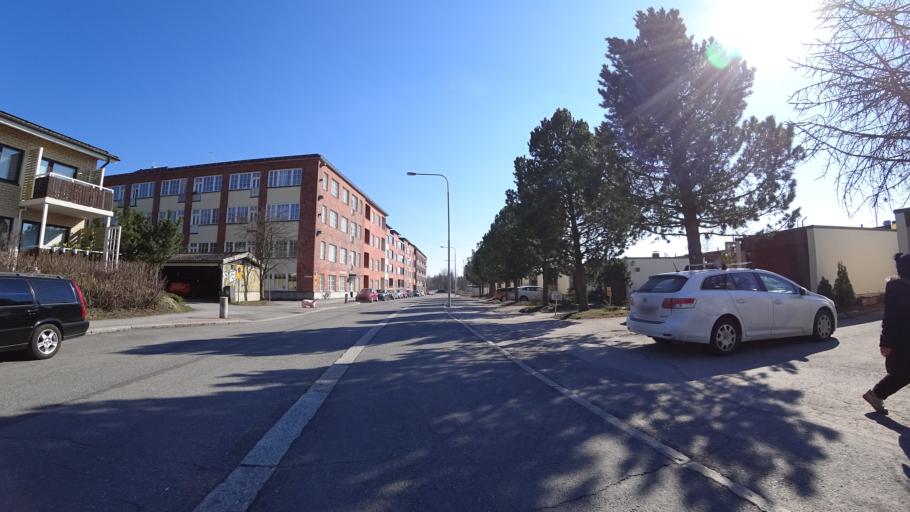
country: FI
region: Pirkanmaa
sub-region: Tampere
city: Pirkkala
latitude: 61.5098
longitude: 23.6624
